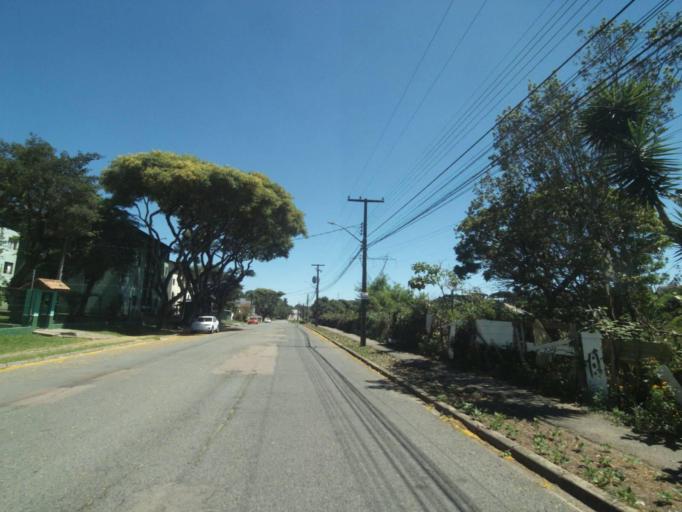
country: BR
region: Parana
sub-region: Curitiba
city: Curitiba
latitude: -25.4735
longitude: -49.3457
